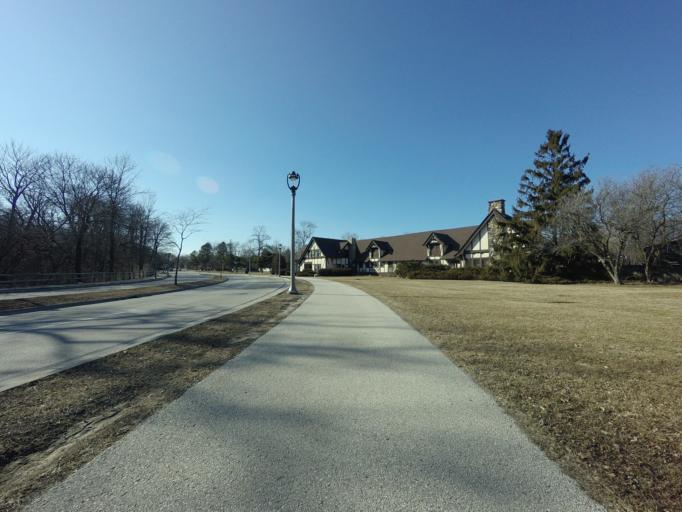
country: US
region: Wisconsin
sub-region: Milwaukee County
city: Shorewood
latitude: 43.0740
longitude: -87.8683
